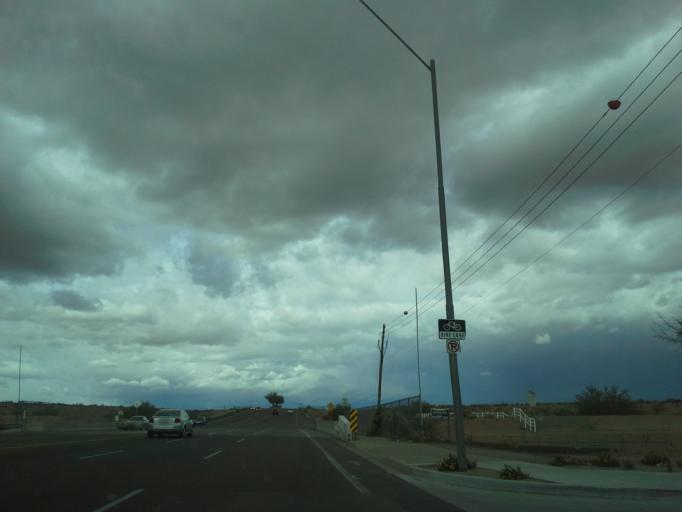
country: US
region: Arizona
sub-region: Maricopa County
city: Paradise Valley
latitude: 33.6556
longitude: -111.9773
